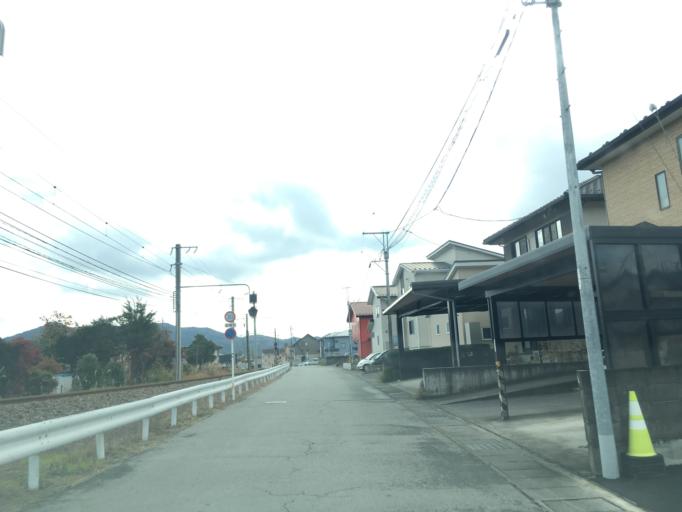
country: JP
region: Yamanashi
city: Fujikawaguchiko
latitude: 35.4861
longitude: 138.7857
